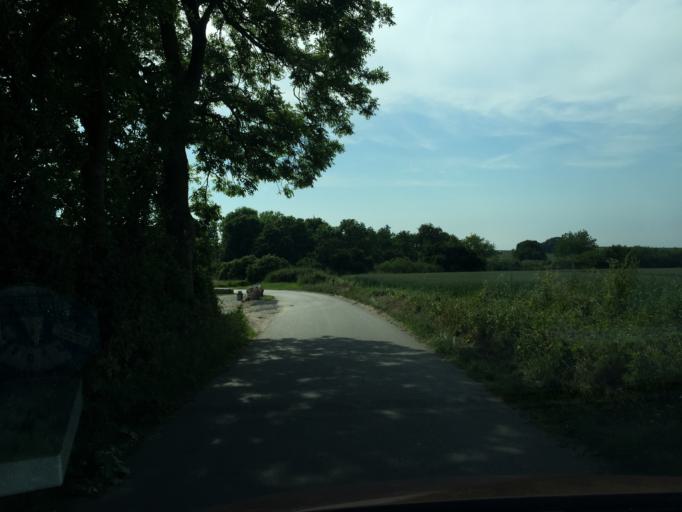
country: DK
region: South Denmark
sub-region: Kerteminde Kommune
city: Kerteminde
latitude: 55.5080
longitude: 10.7078
